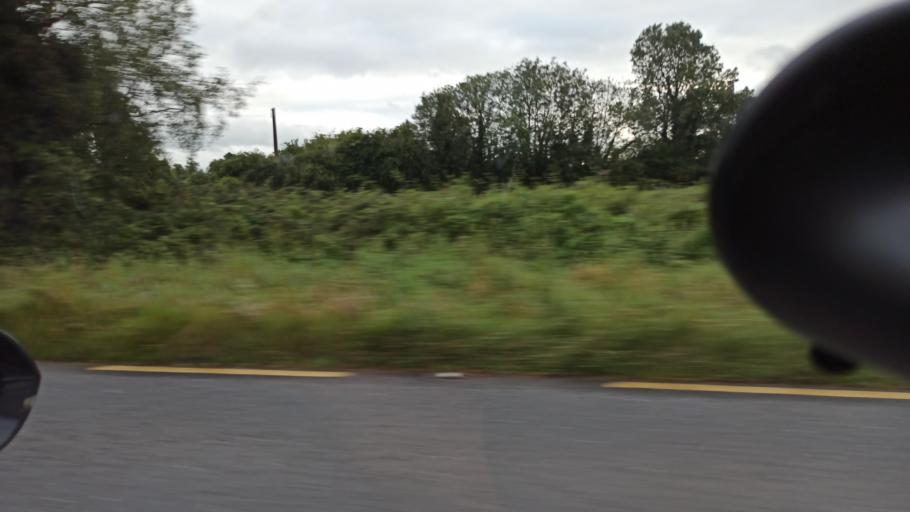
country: IE
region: Munster
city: Thurles
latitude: 52.6937
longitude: -7.8126
